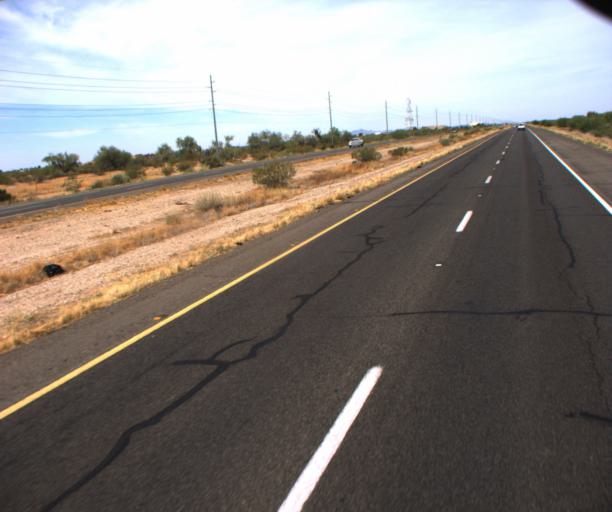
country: US
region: Arizona
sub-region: Maricopa County
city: Sun City West
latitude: 33.7293
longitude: -112.4661
